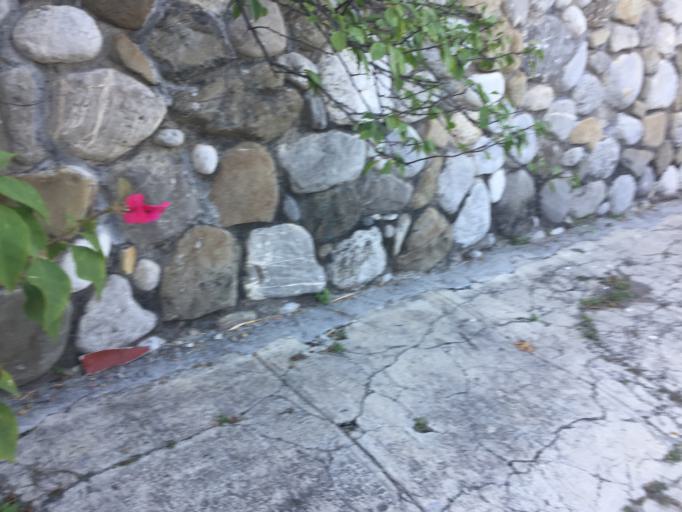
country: MX
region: Nuevo Leon
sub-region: San Pedro Garza Garcia
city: San Pedro Garza Garcia
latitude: 25.6561
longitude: -100.3952
